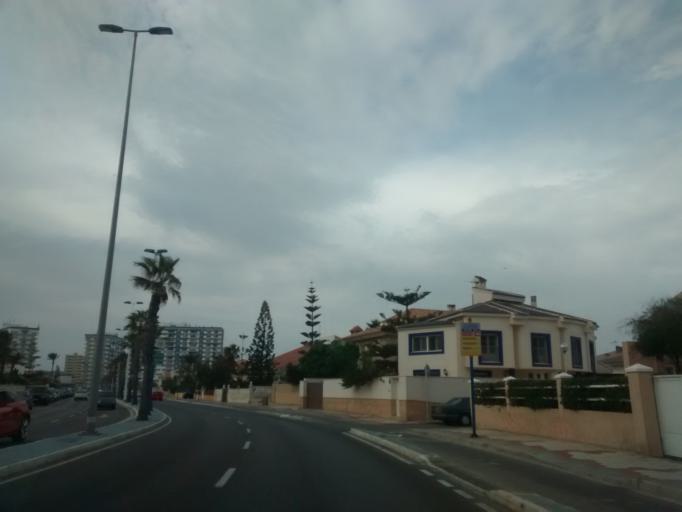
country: ES
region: Murcia
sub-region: Murcia
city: La Manga del Mar Menor
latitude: 37.6824
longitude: -0.7344
